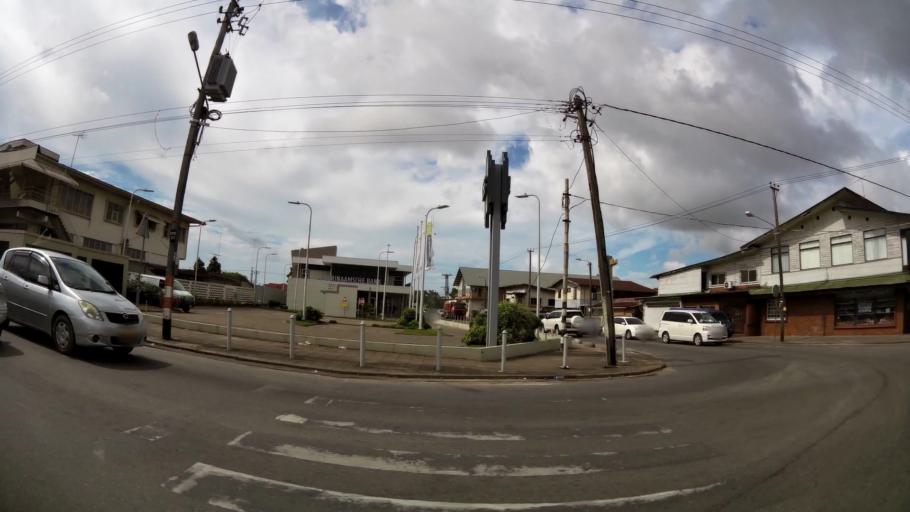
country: SR
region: Paramaribo
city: Paramaribo
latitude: 5.8401
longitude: -55.1847
